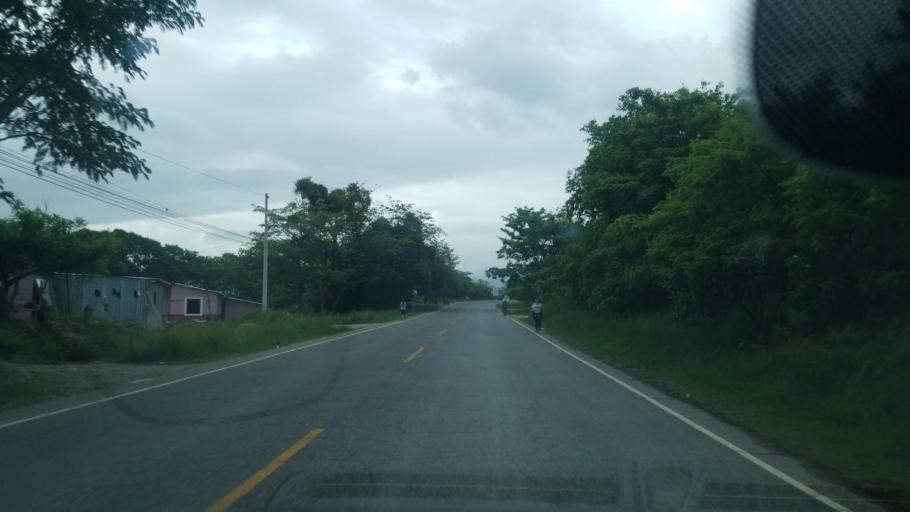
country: HN
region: Ocotepeque
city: Santa Lucia
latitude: 14.4147
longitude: -89.1944
